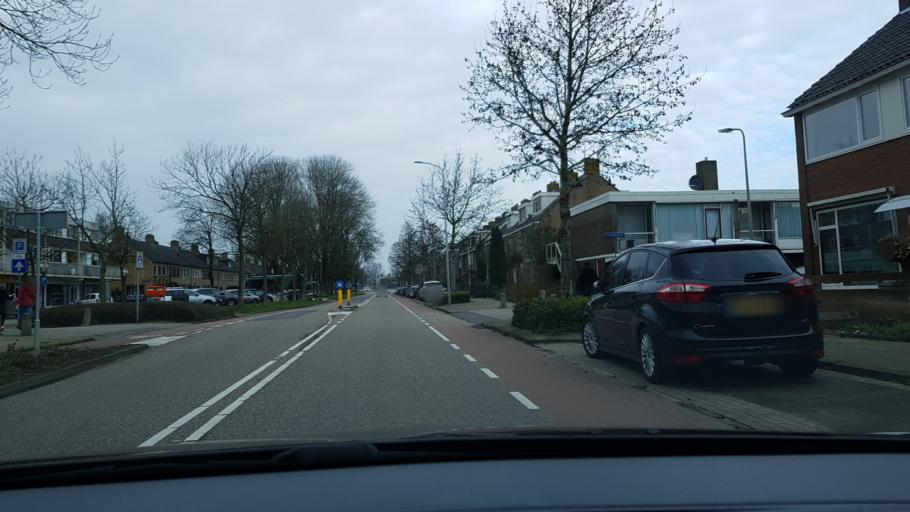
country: NL
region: North Holland
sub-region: Gemeente Uithoorn
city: Uithoorn
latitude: 52.2496
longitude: 4.8274
